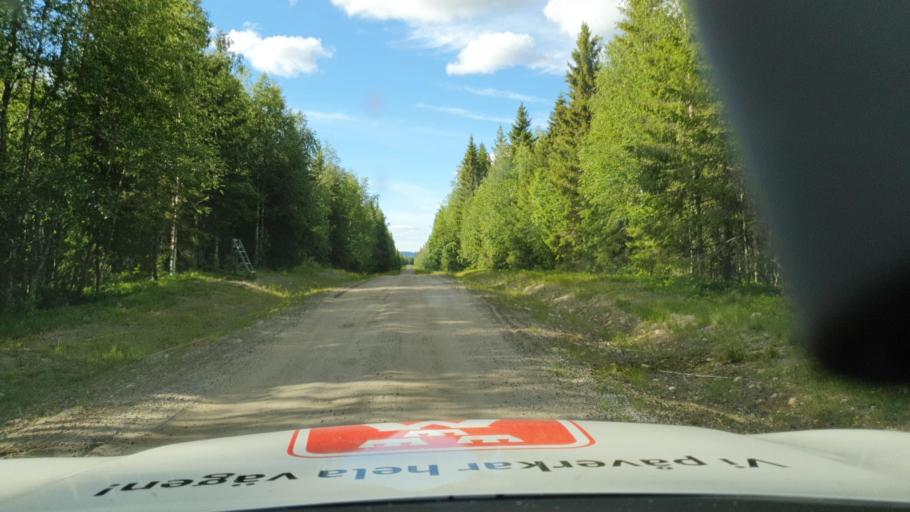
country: SE
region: Vaesterbotten
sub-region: Lycksele Kommun
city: Lycksele
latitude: 64.4305
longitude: 18.2746
